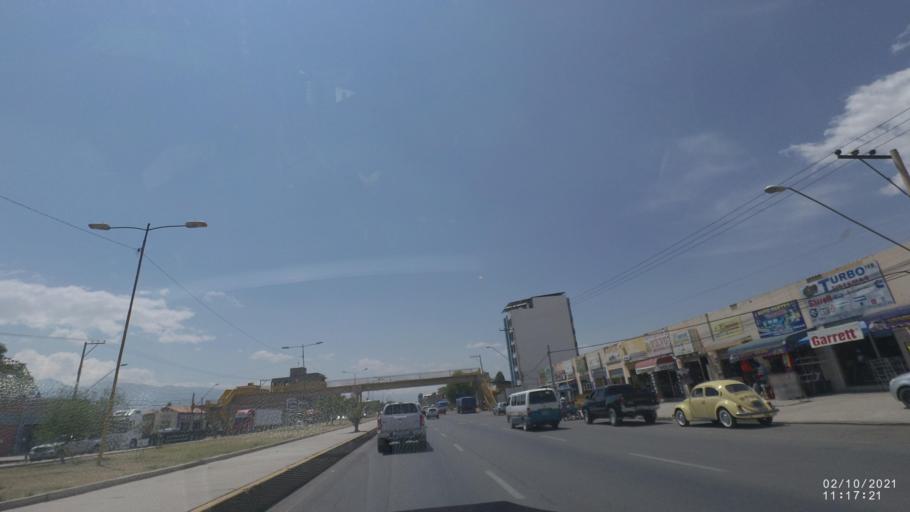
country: BO
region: Cochabamba
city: Sipe Sipe
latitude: -17.3947
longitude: -66.2906
